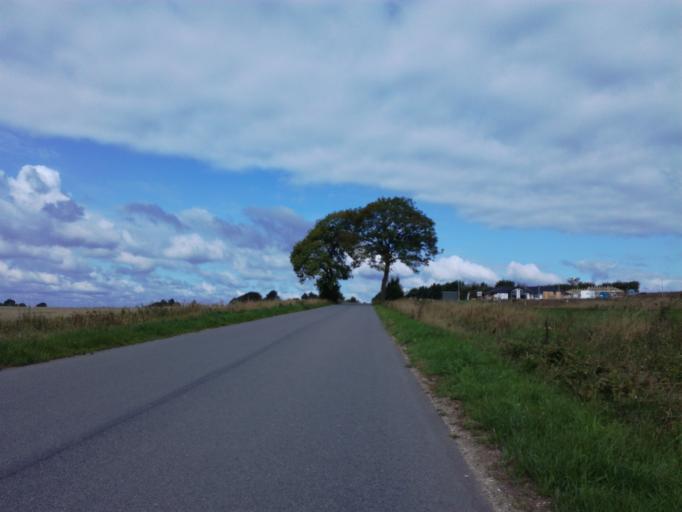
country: DK
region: South Denmark
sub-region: Vejle Kommune
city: Vejle
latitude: 55.6665
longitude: 9.5803
